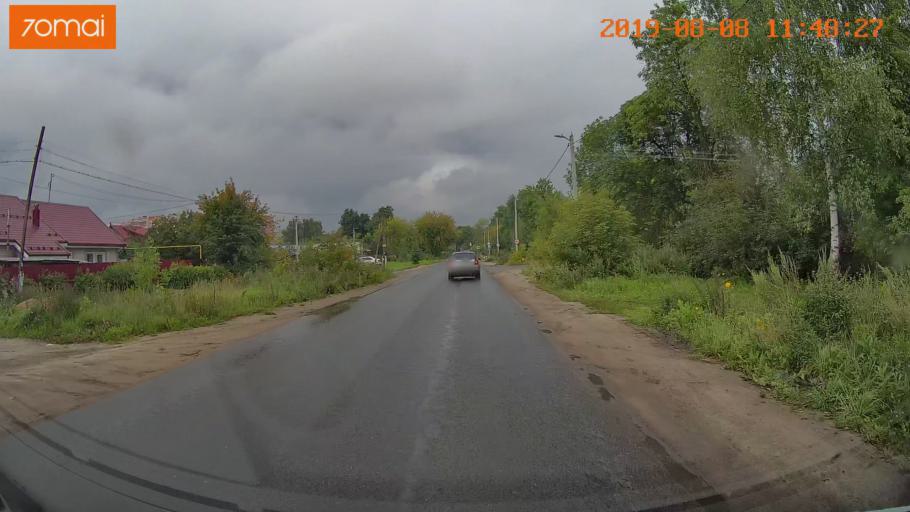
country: RU
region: Ivanovo
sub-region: Gorod Ivanovo
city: Ivanovo
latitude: 56.9728
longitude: 40.9835
